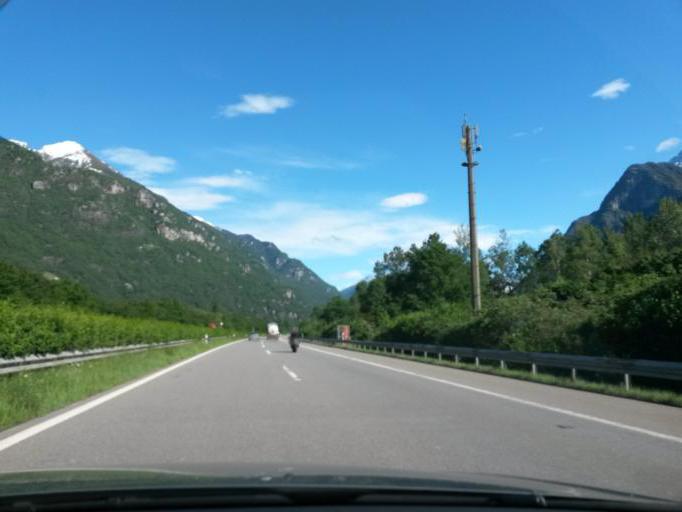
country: CH
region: Ticino
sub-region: Riviera District
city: Claro
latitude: 46.2718
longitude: 9.0003
